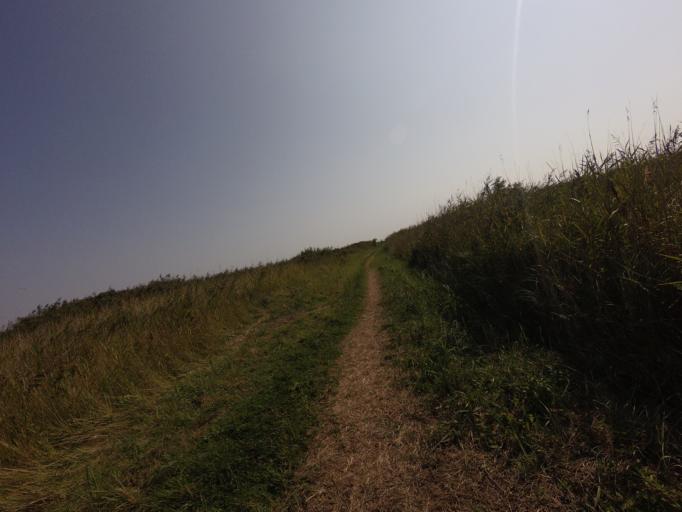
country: NL
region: Friesland
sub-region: Gemeente Schiermonnikoog
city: Schiermonnikoog
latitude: 53.4954
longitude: 6.2433
